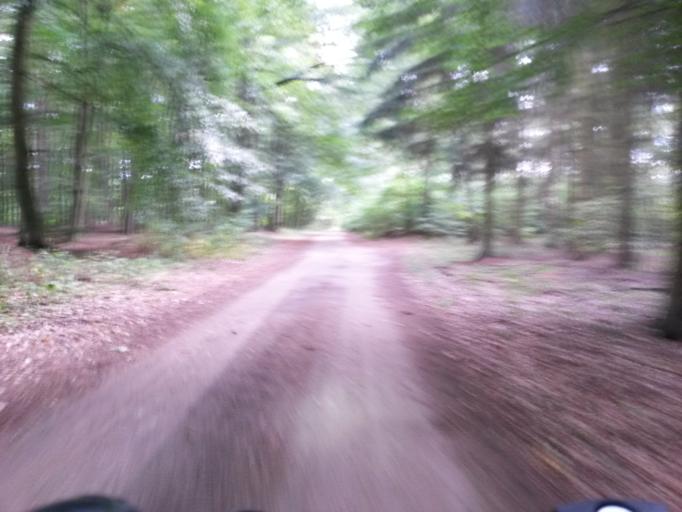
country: DE
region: Brandenburg
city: Templin
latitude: 53.0889
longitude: 13.5379
